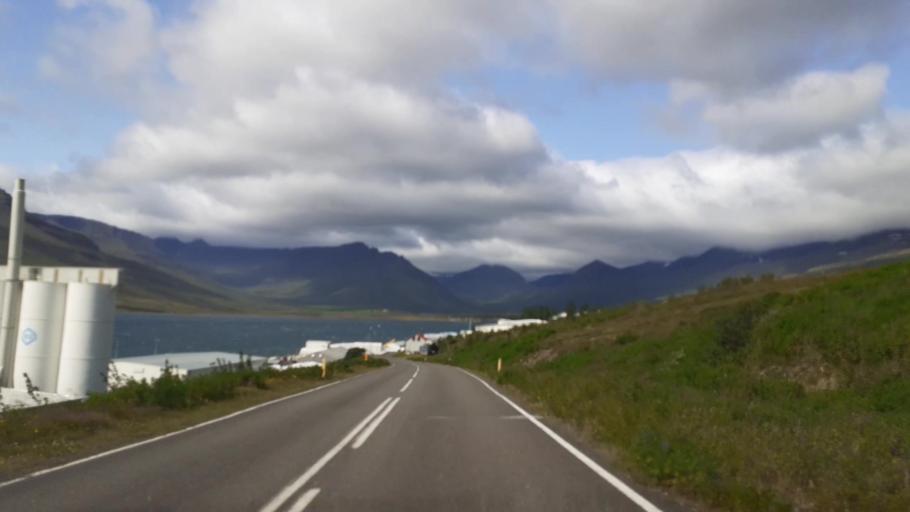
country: IS
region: East
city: Eskifjoerdur
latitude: 64.9247
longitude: -13.9885
